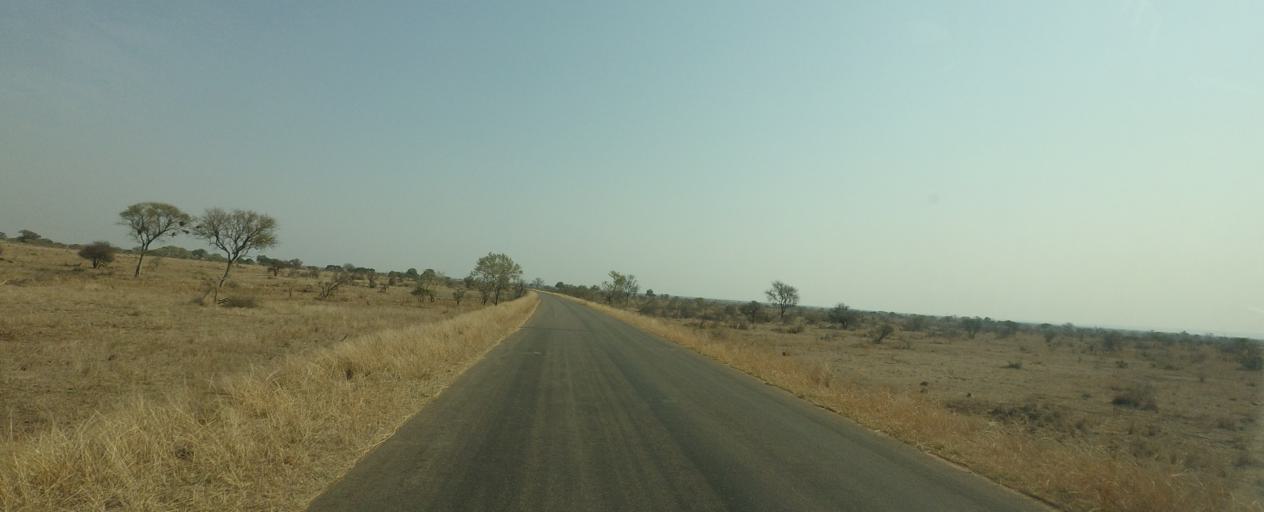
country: ZA
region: Limpopo
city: Thulamahashi
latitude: -24.3147
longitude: 31.7488
